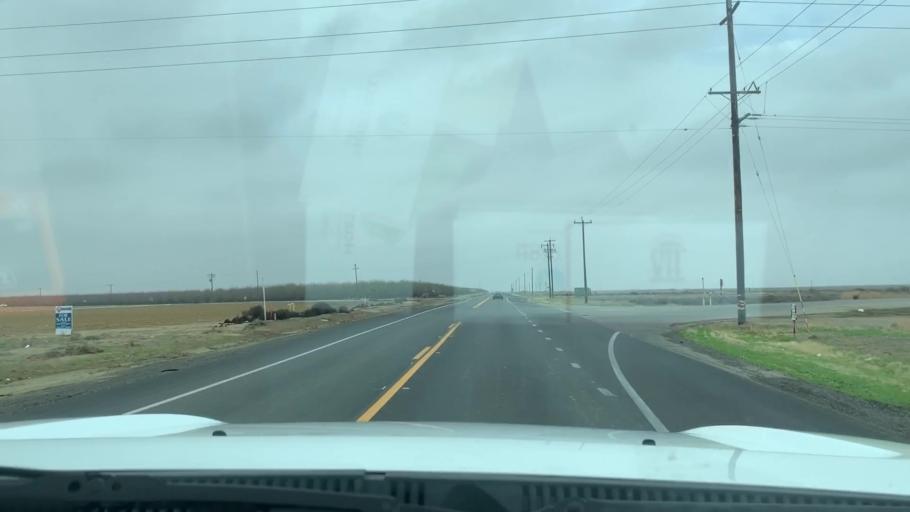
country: US
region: California
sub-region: Kern County
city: Lost Hills
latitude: 35.6158
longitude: -119.7426
